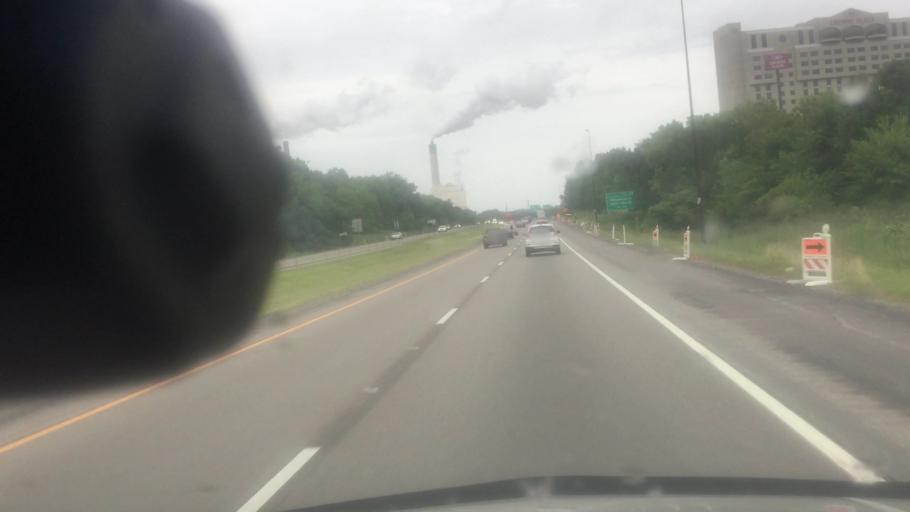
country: US
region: Illinois
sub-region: Sangamon County
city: Southern View
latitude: 39.7673
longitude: -89.6042
